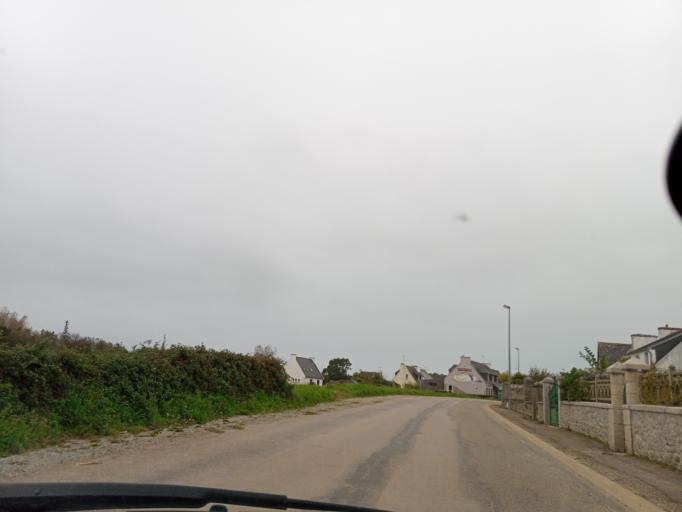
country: FR
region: Brittany
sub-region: Departement du Finistere
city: Esquibien
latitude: 48.0244
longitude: -4.5575
